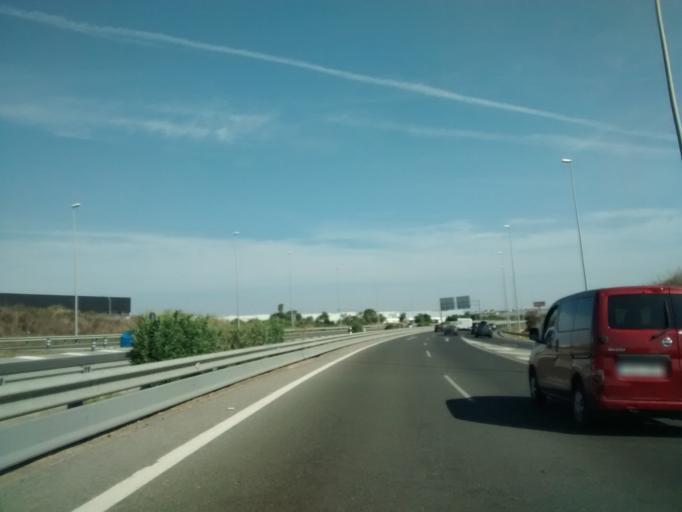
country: ES
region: Andalusia
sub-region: Provincia de Cadiz
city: Chiclana de la Frontera
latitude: 36.4009
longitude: -6.1263
